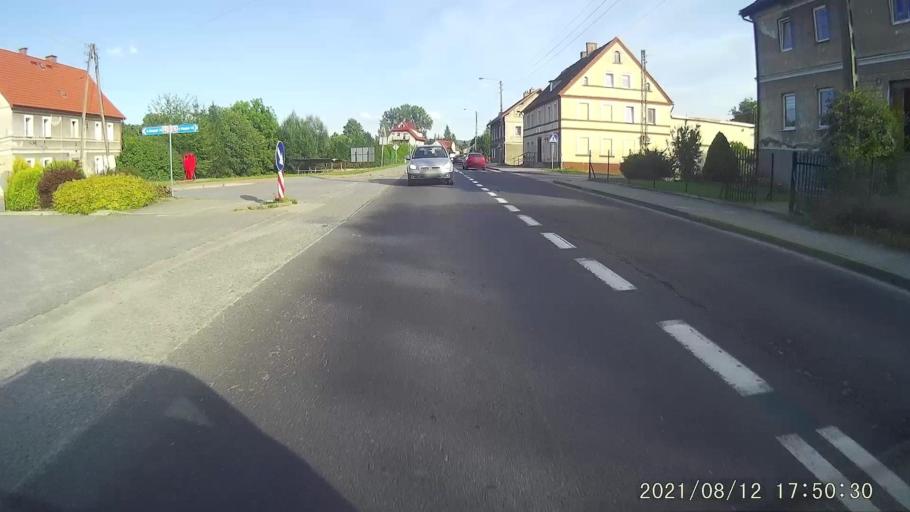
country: PL
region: Lower Silesian Voivodeship
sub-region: Powiat klodzki
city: Klodzko
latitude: 50.3667
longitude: 16.7090
